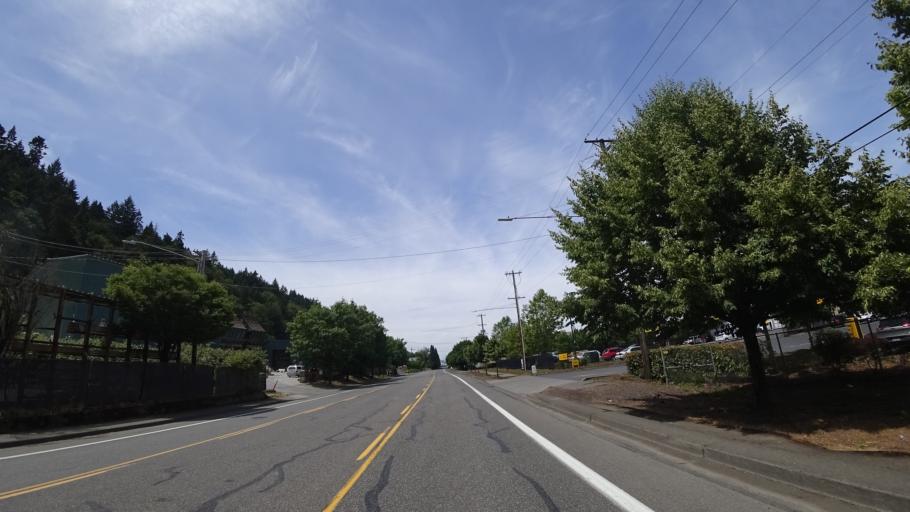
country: US
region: Oregon
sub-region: Washington County
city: West Haven-Sylvan
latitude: 45.5517
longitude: -122.7299
